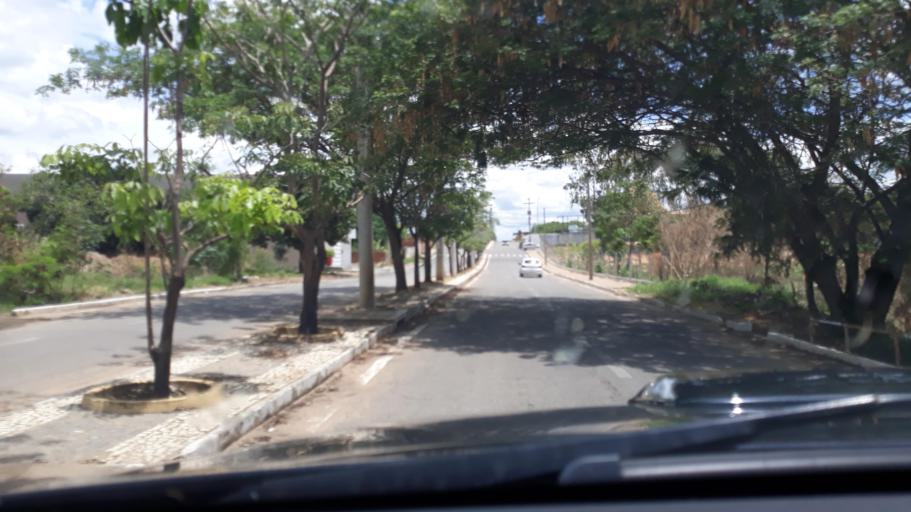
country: BR
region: Bahia
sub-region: Guanambi
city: Guanambi
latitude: -14.2280
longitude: -42.7678
